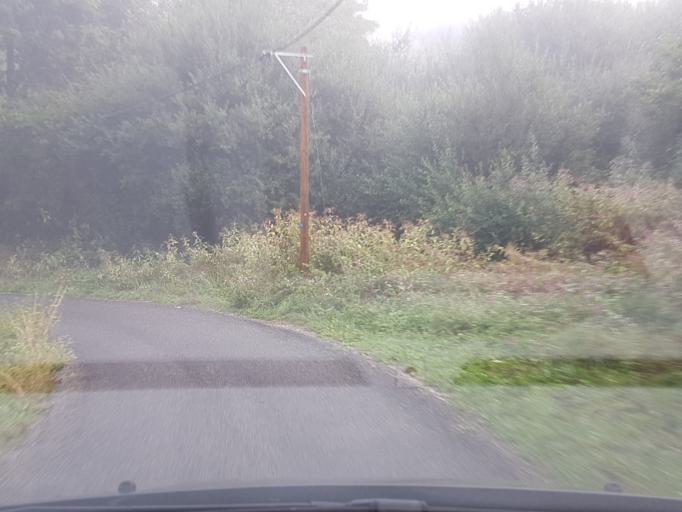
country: FR
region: Midi-Pyrenees
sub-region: Departement de l'Ariege
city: Montjoie-en-Couserans
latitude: 42.9022
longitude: 1.3550
